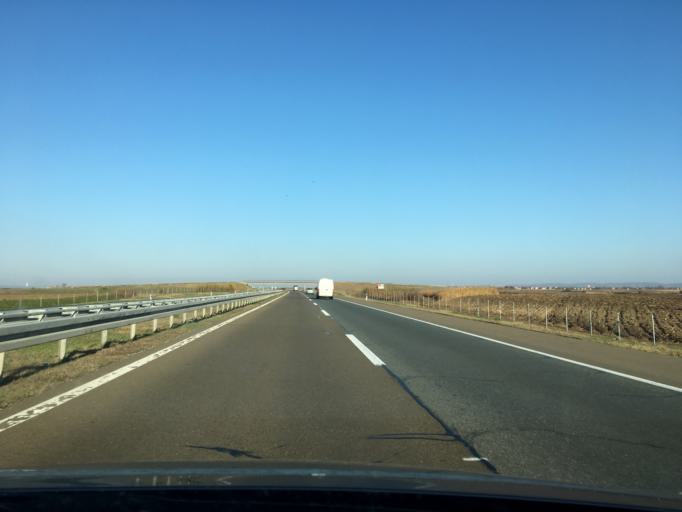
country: RS
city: Novi Karlovci
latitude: 45.0441
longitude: 20.1790
